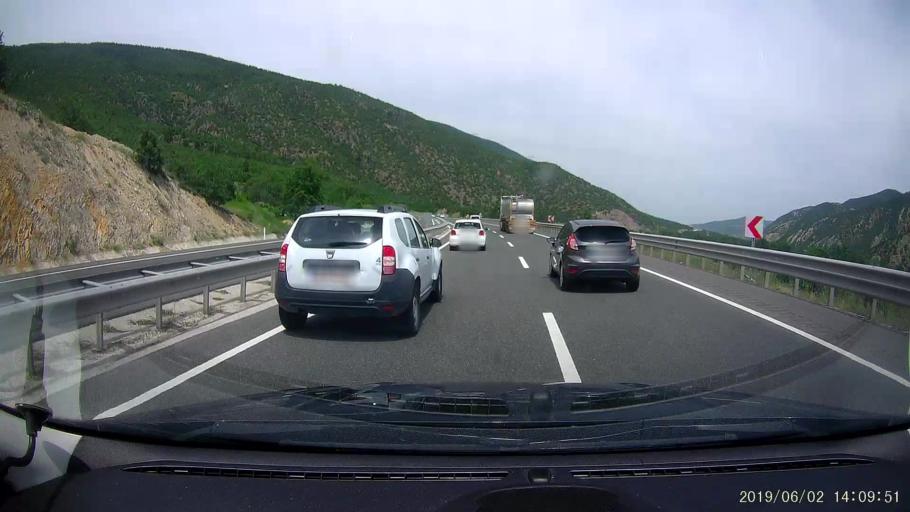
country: TR
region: Cankiri
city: Ilgaz
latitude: 40.8981
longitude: 33.7491
